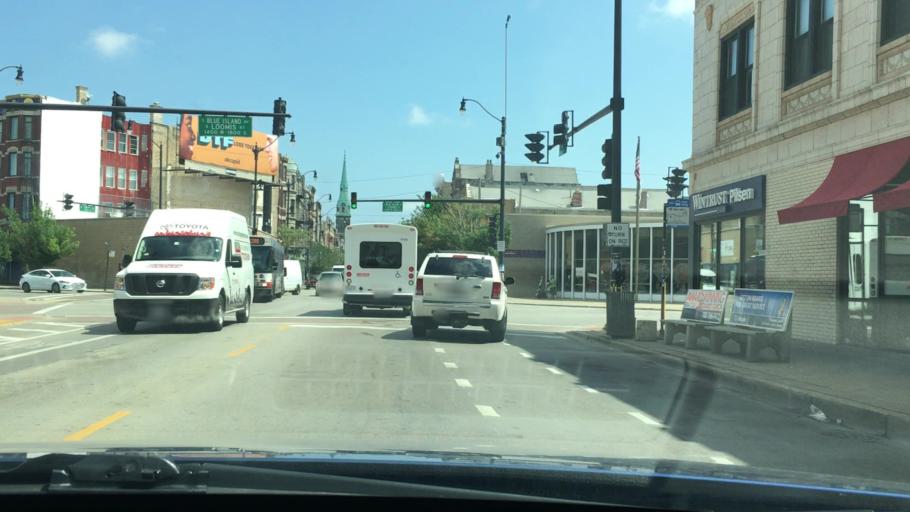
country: US
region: Illinois
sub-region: Cook County
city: Chicago
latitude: 41.8579
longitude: -87.6617
